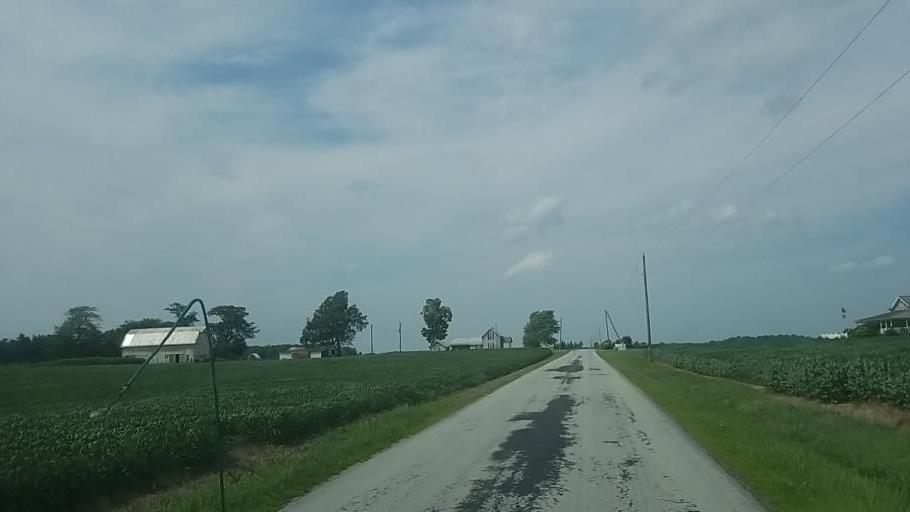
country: US
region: Ohio
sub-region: Hardin County
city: Forest
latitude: 40.7671
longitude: -83.5572
